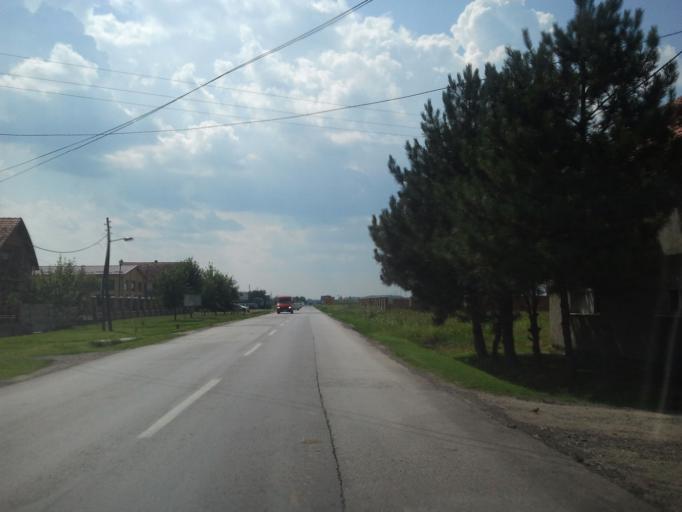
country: RS
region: Autonomna Pokrajina Vojvodina
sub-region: Juznobacki Okrug
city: Beocin
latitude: 45.2398
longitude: 19.6782
